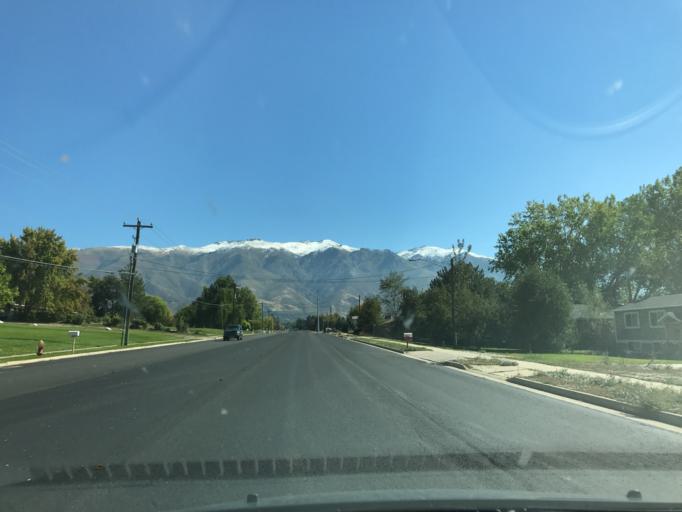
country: US
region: Utah
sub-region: Davis County
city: Hill Air Force Bace
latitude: 41.0890
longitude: -111.9563
